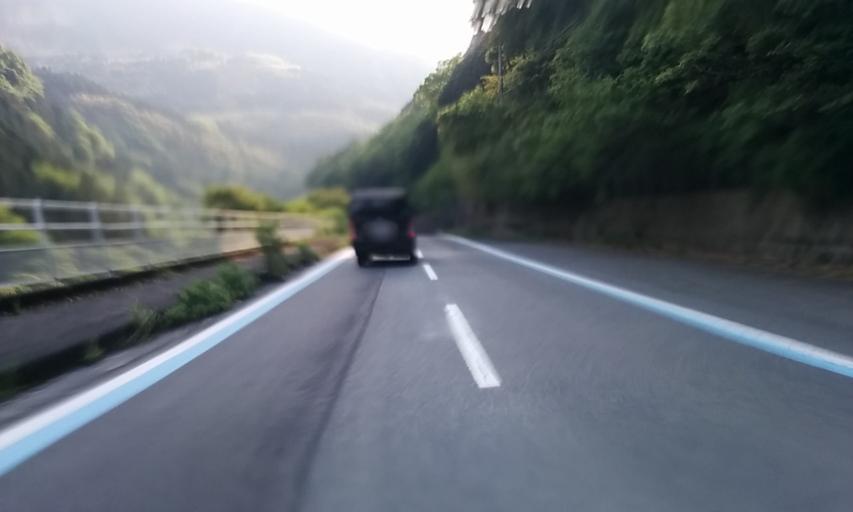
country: JP
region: Ehime
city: Saijo
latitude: 33.8663
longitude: 133.1900
